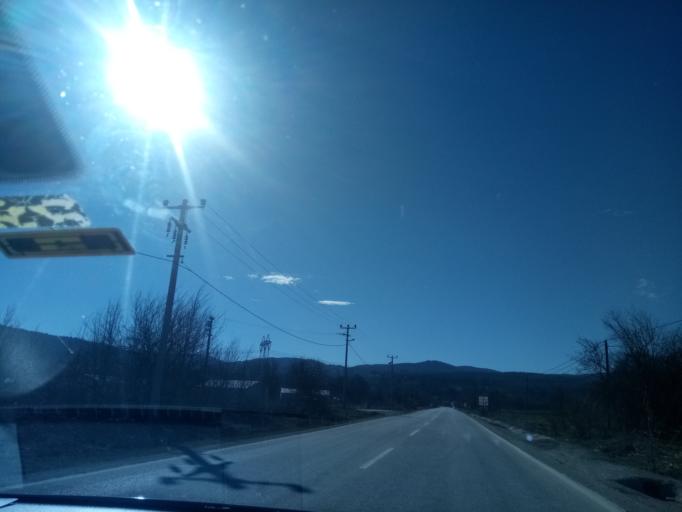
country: TR
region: Duzce
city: Kaynasli
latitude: 40.7016
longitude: 31.4527
